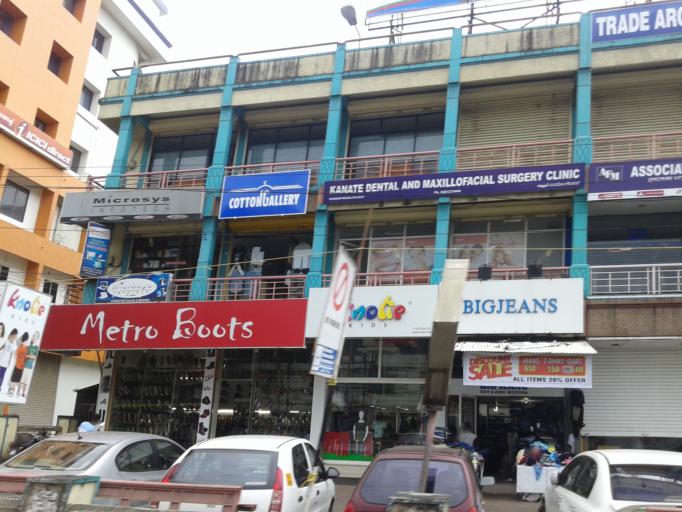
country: IN
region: Kerala
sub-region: Kozhikode
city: Kozhikode
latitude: 11.2600
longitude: 75.7772
